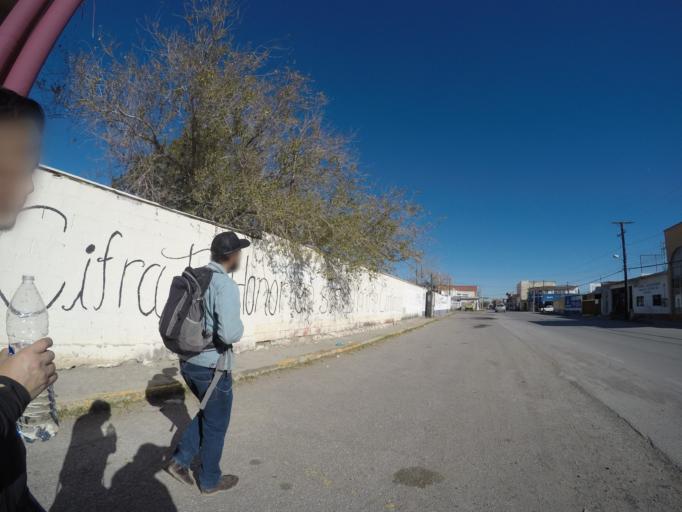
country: MX
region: Chihuahua
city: Ciudad Juarez
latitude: 31.7346
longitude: -106.4577
